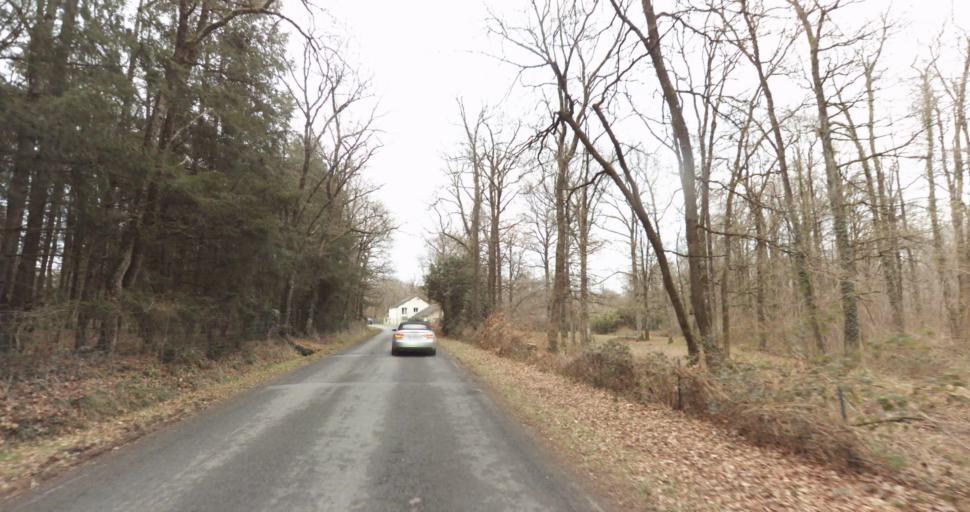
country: FR
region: Pays de la Loire
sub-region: Departement de Maine-et-Loire
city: Distre
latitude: 47.2549
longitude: -0.1260
